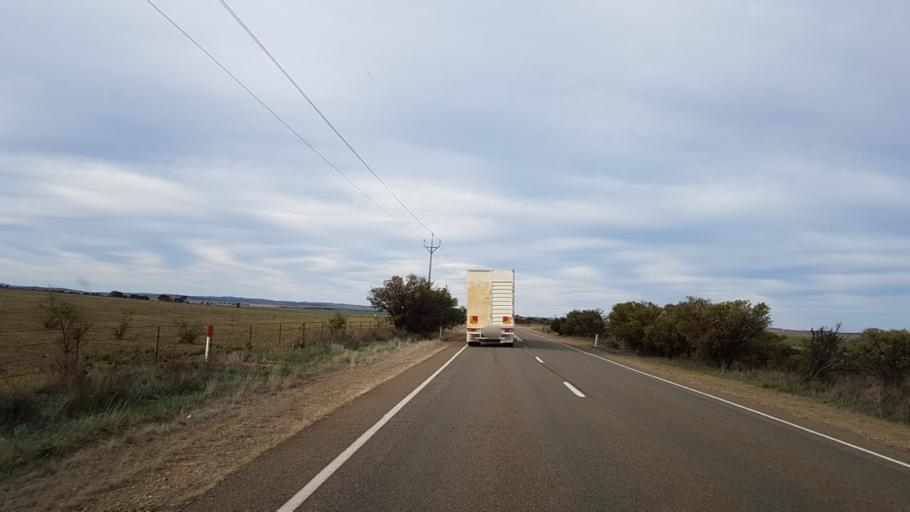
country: AU
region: South Australia
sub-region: Peterborough
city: Peterborough
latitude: -33.0171
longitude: 138.7568
